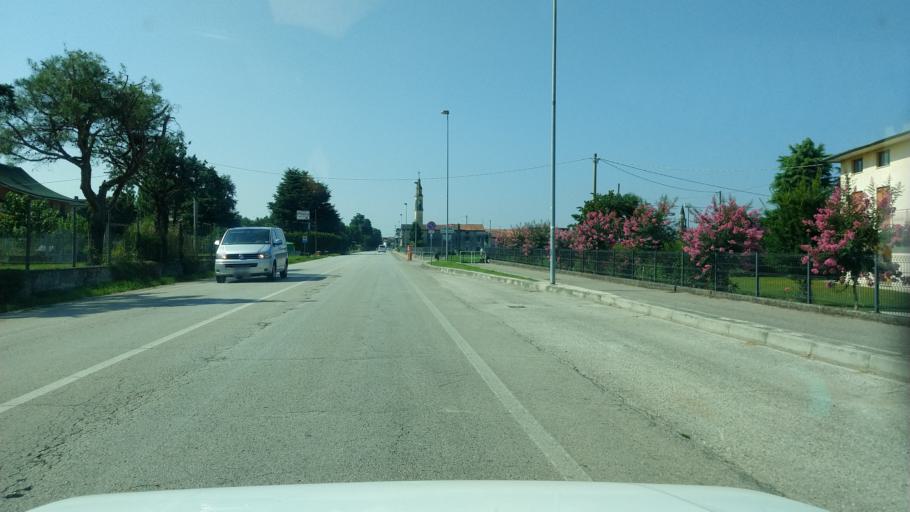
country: IT
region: Veneto
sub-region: Provincia di Vicenza
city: Schiavon
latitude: 45.6861
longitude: 11.6413
